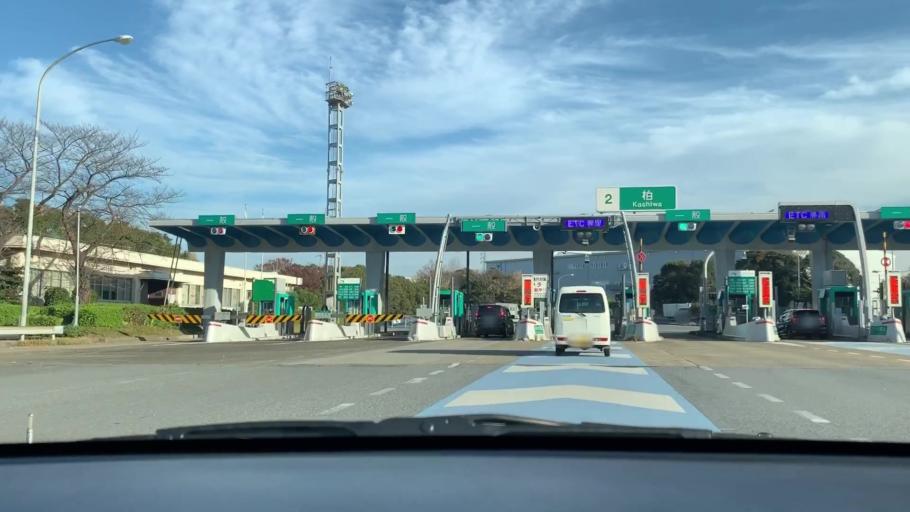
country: JP
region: Chiba
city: Nagareyama
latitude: 35.9080
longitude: 139.9370
